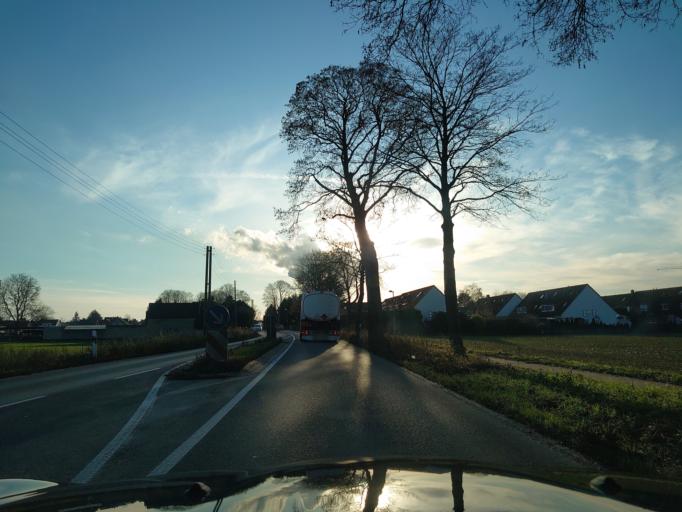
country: DE
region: North Rhine-Westphalia
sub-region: Regierungsbezirk Dusseldorf
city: Rommerskirchen
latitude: 51.0530
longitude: 6.7150
